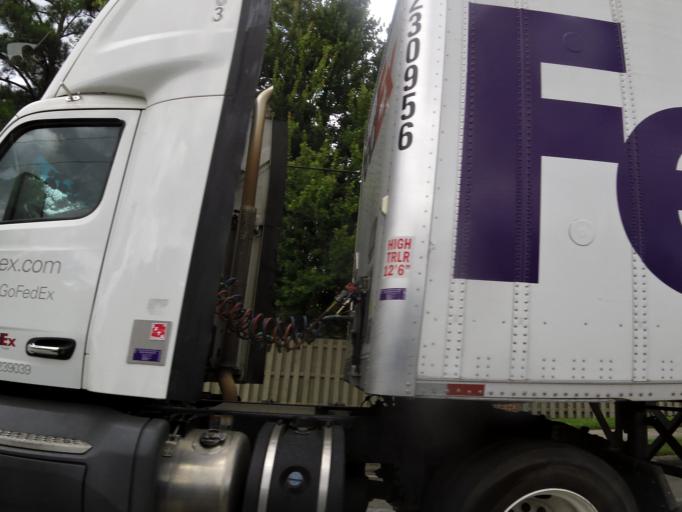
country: US
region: Florida
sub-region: Clay County
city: Lakeside
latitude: 30.1006
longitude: -81.7588
